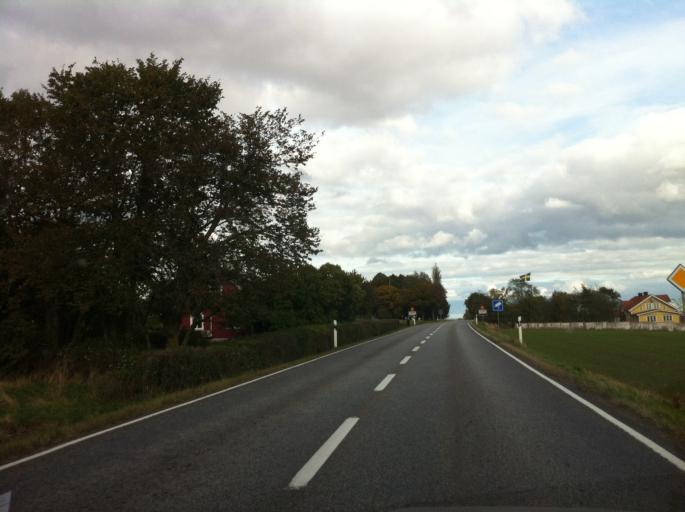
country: SE
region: OEstergoetland
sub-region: Vadstena Kommun
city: Herrestad
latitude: 58.3629
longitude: 14.7205
